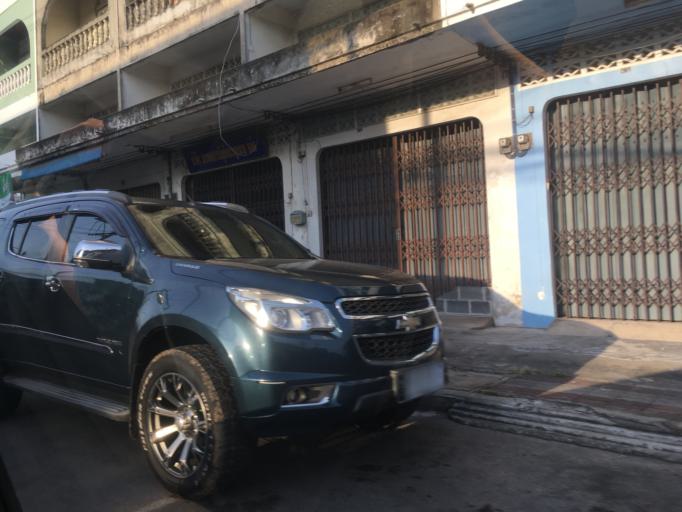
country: TH
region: Pattani
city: Pattani
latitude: 6.8601
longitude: 101.2516
